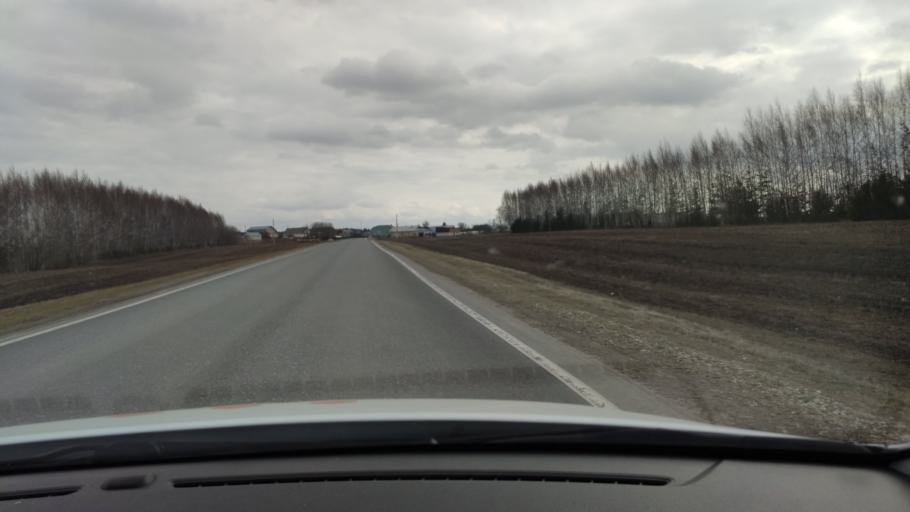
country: RU
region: Tatarstan
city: Vysokaya Gora
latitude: 56.1765
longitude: 49.2128
